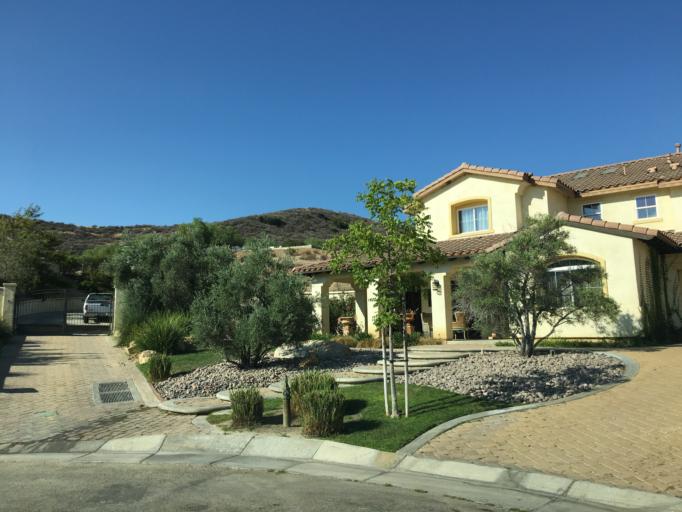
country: US
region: California
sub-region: Los Angeles County
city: Val Verde
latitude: 34.4639
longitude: -118.6710
